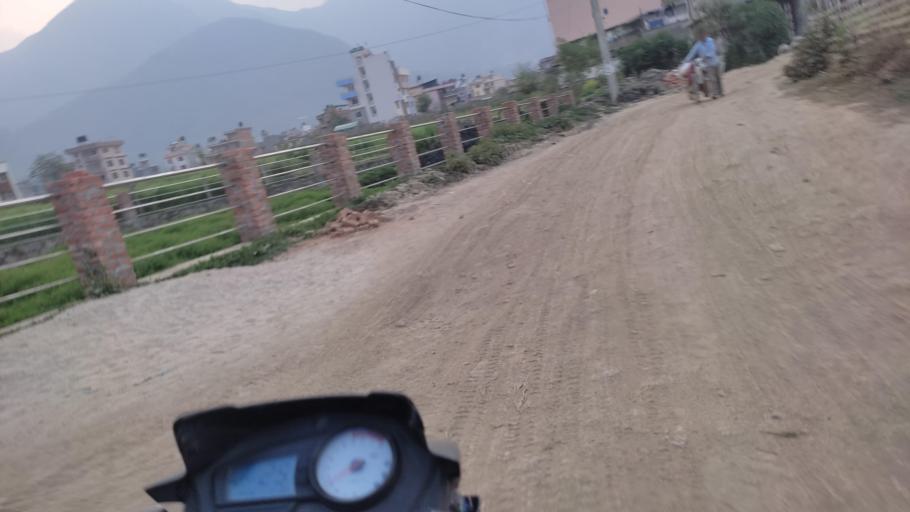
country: NP
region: Central Region
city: Kirtipur
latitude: 27.6677
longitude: 85.2773
